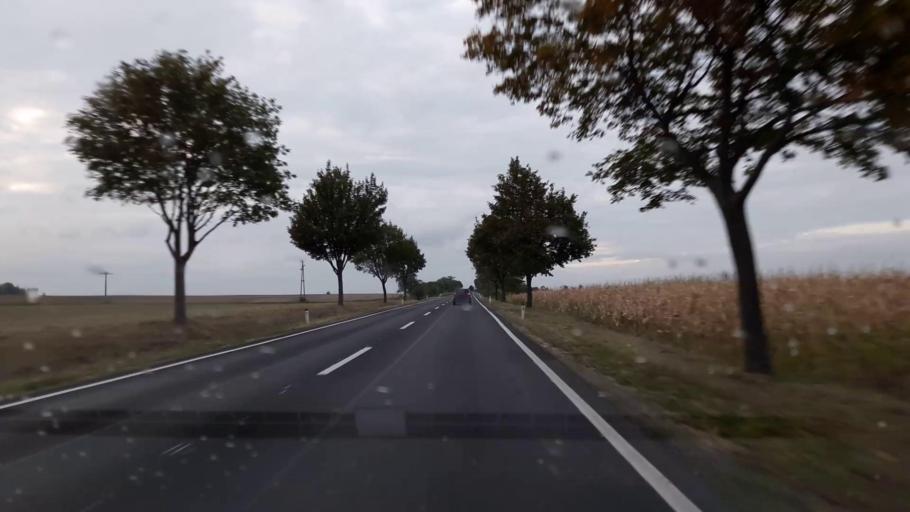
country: AT
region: Lower Austria
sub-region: Politischer Bezirk Wien-Umgebung
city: Schwadorf
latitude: 48.0803
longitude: 16.5693
